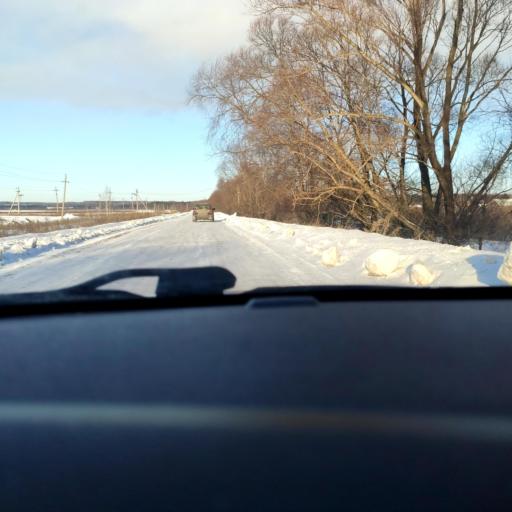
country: RU
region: Bashkortostan
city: Mikhaylovka
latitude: 54.7732
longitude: 55.8280
